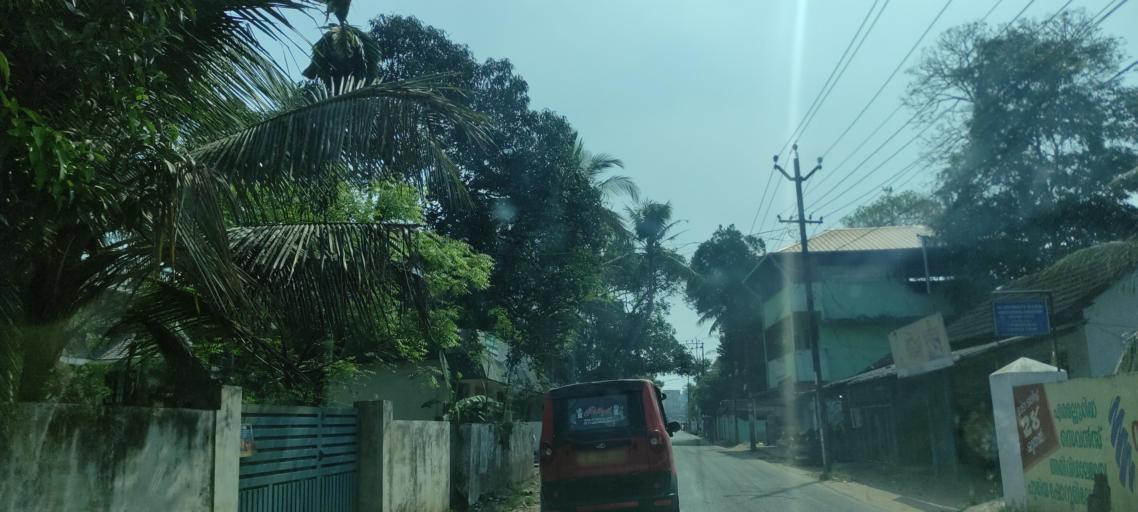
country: IN
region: Kerala
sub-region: Alappuzha
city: Kutiatodu
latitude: 9.8234
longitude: 76.3085
